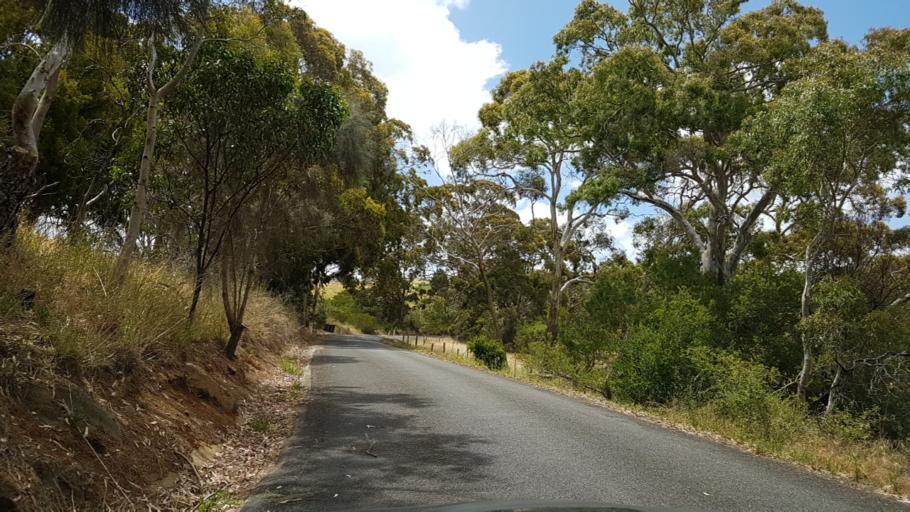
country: AU
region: South Australia
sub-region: Victor Harbor
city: Victor Harbor
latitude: -35.4592
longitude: 138.5918
